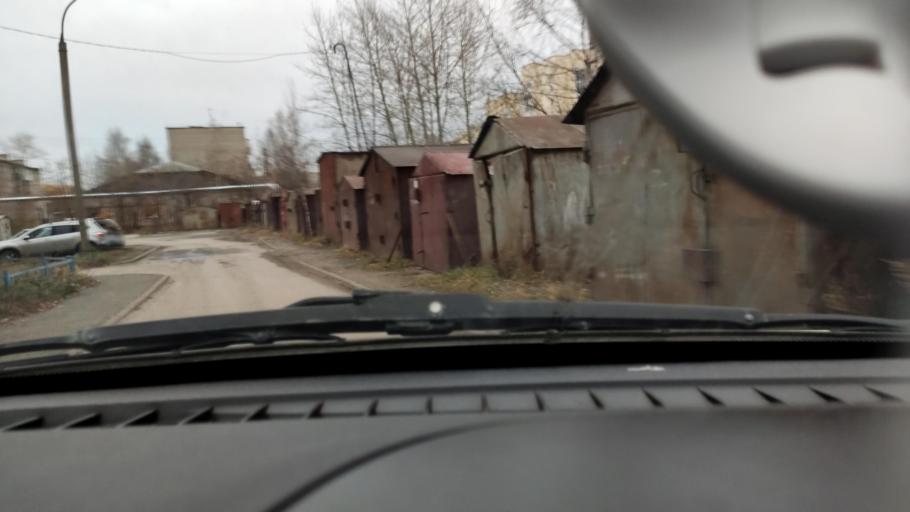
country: RU
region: Perm
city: Kondratovo
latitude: 58.0015
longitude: 56.1105
